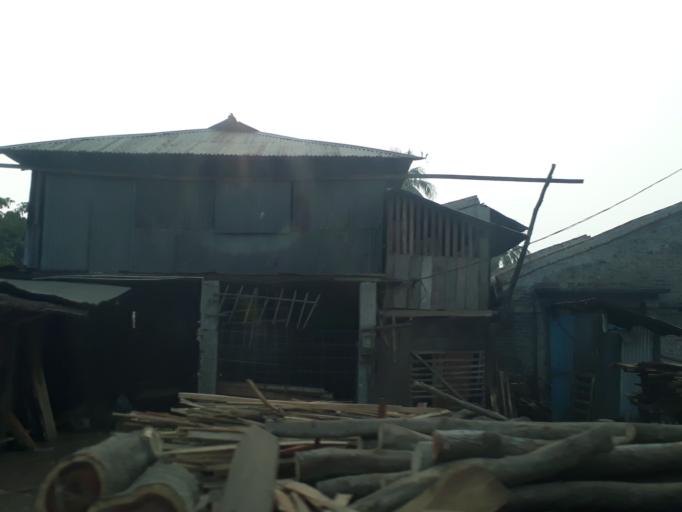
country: BD
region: Khulna
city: Khulna
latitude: 22.8841
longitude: 89.5168
